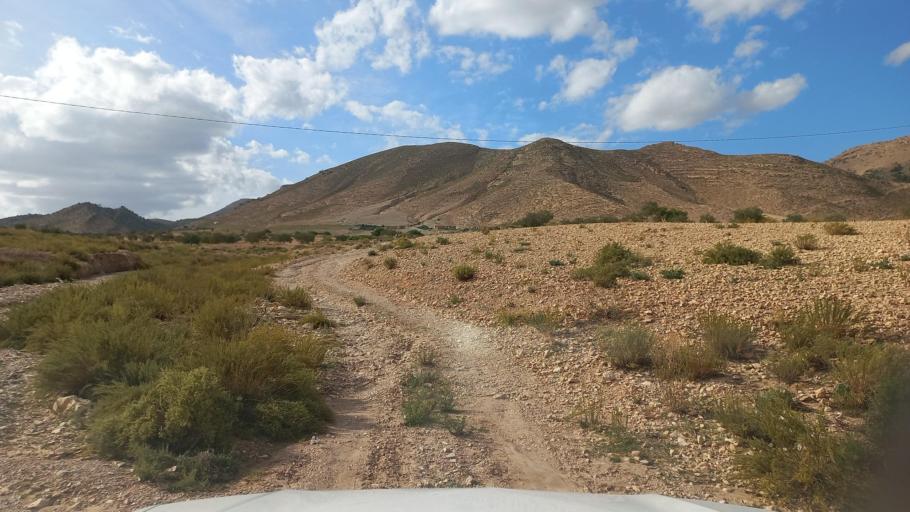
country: TN
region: Al Qasrayn
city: Sbiba
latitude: 35.4543
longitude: 9.0728
